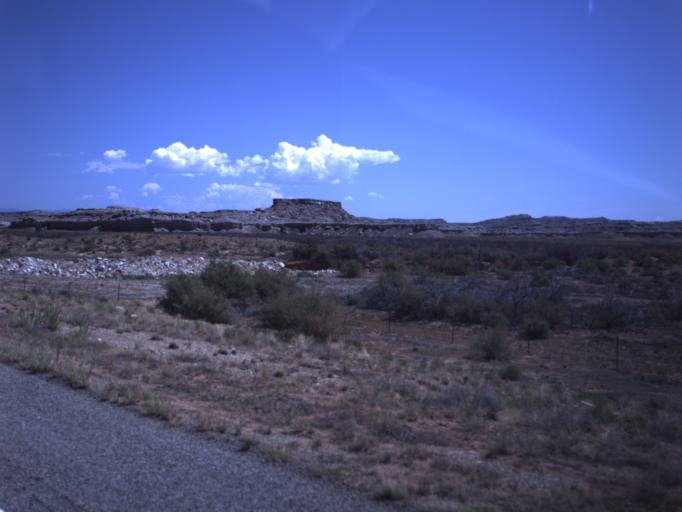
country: US
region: Utah
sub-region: Carbon County
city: East Carbon City
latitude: 38.8433
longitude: -110.3816
